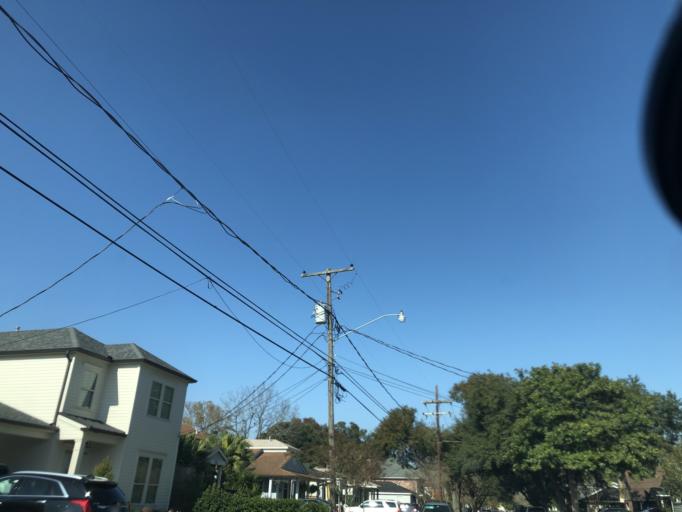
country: US
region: Louisiana
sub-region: Jefferson Parish
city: Metairie
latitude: 29.9881
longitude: -90.1525
